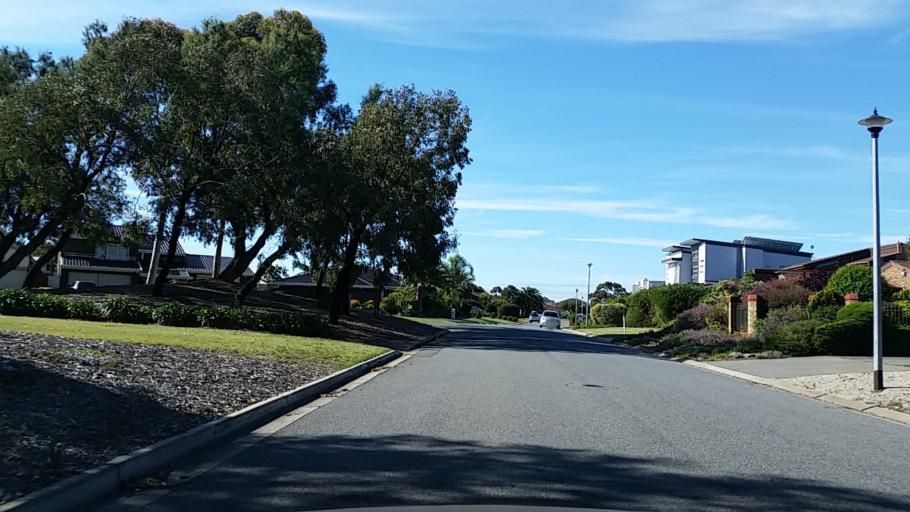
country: AU
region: South Australia
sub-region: Charles Sturt
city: West Lakes Shore
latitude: -34.8693
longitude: 138.4922
